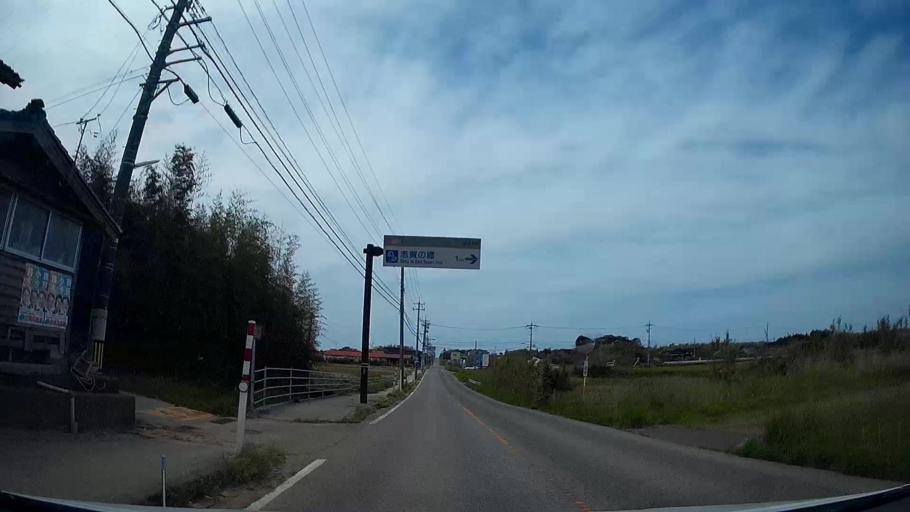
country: JP
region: Ishikawa
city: Hakui
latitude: 37.0124
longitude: 136.7591
